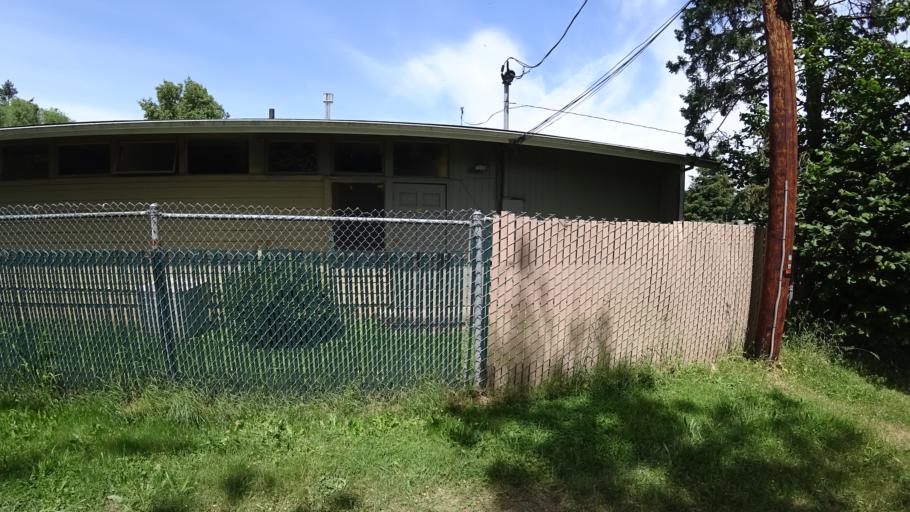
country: US
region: Oregon
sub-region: Multnomah County
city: Lents
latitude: 45.4659
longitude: -122.5989
